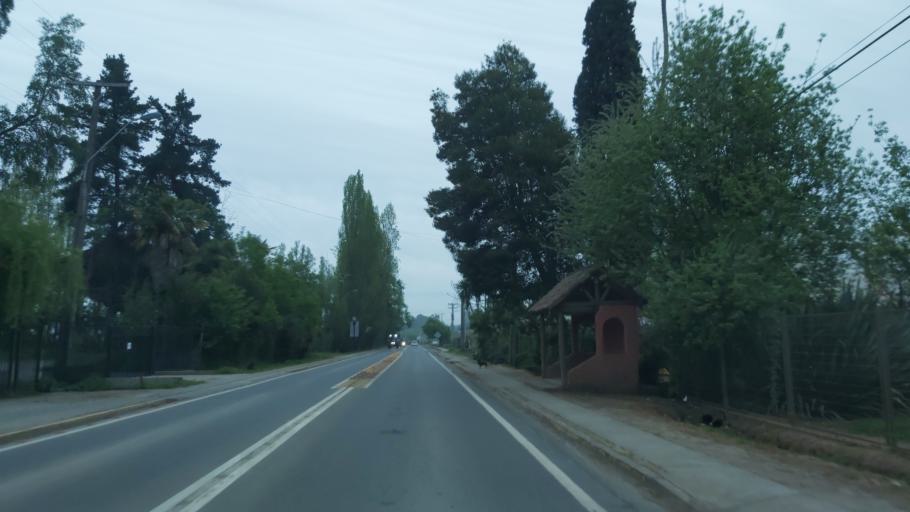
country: CL
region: Maule
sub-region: Provincia de Linares
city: Colbun
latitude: -35.7548
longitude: -71.4987
